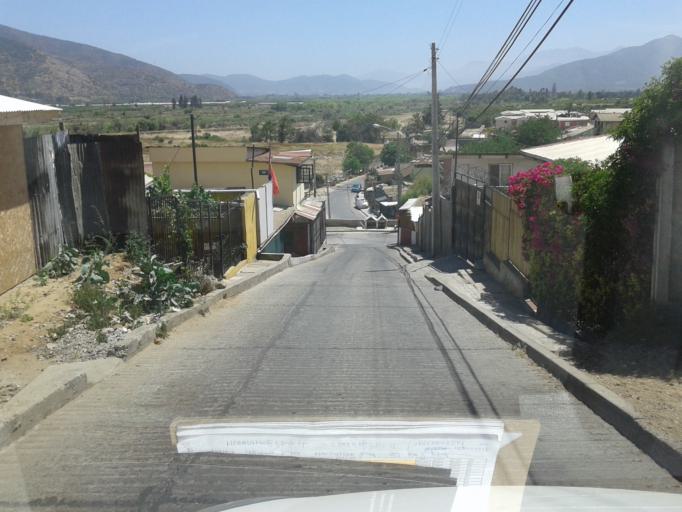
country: CL
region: Valparaiso
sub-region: Provincia de Quillota
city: Quillota
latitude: -32.8730
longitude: -71.2470
